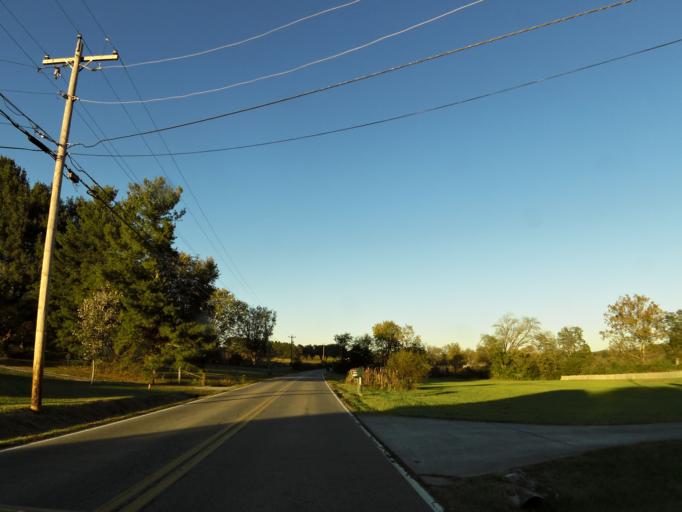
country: US
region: Tennessee
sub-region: Blount County
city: Wildwood
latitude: 35.7999
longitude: -83.8109
